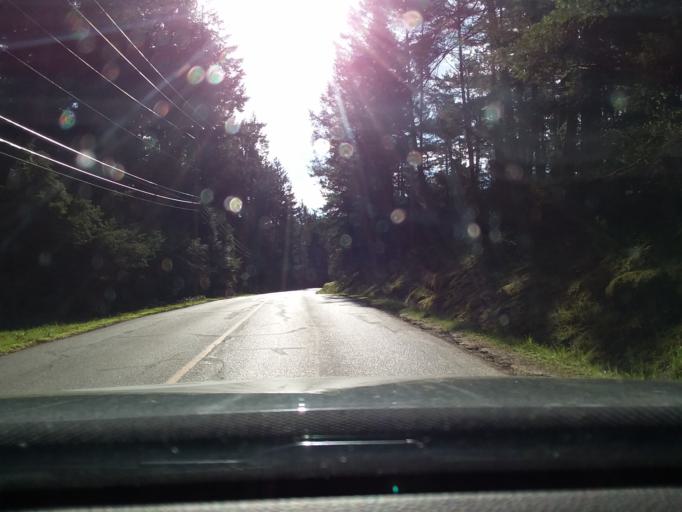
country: CA
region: British Columbia
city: North Saanich
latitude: 48.8879
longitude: -123.3357
